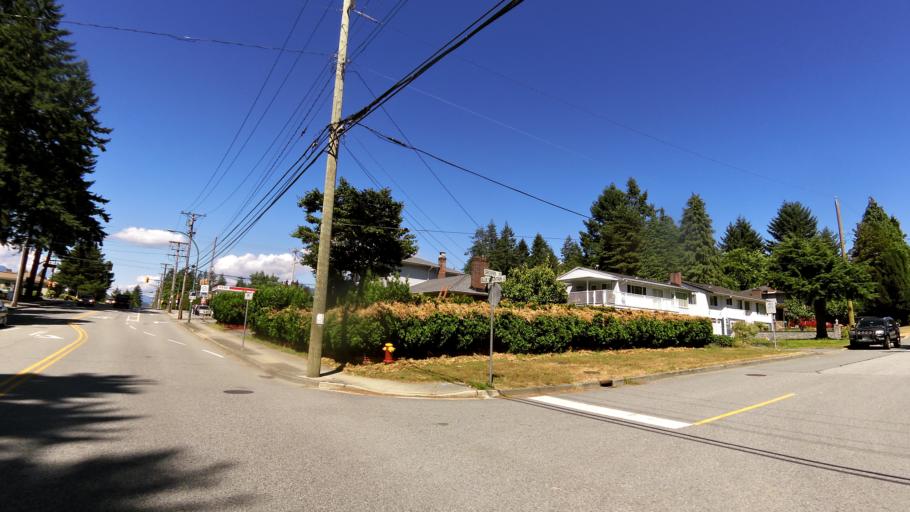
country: CA
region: British Columbia
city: Port Moody
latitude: 49.2626
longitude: -122.8686
